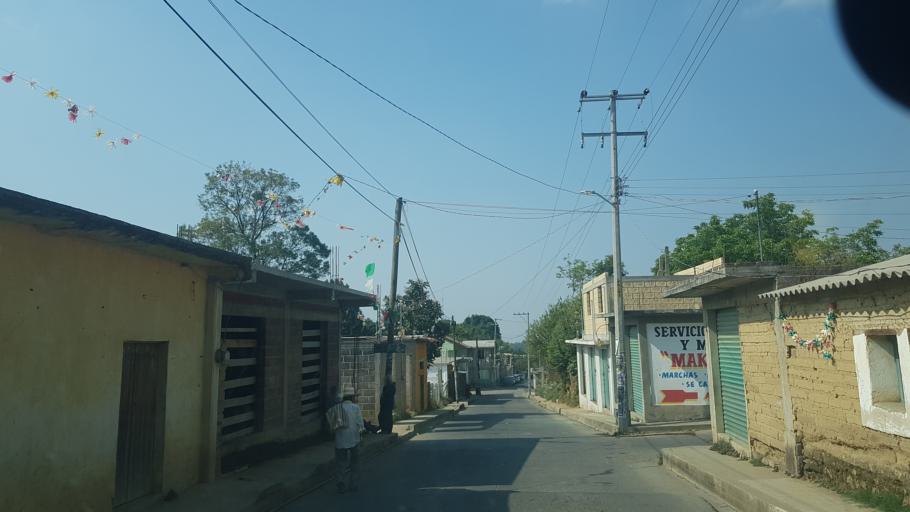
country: MX
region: Morelos
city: Hueyapan
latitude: 18.8859
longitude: -98.6887
